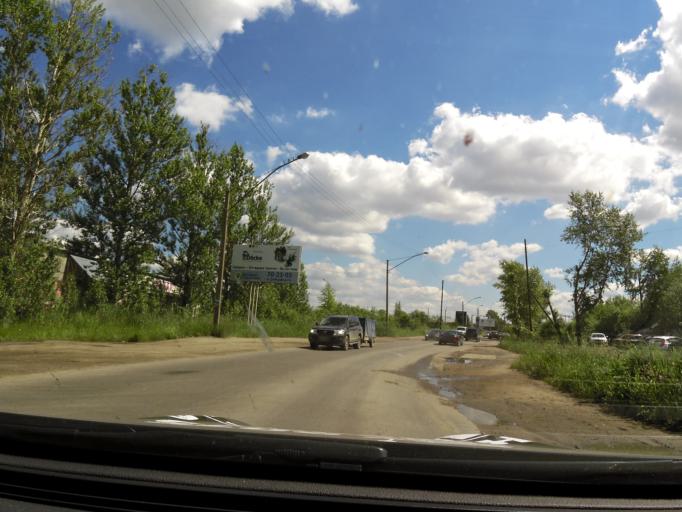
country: RU
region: Vologda
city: Vologda
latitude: 59.2345
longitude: 39.8332
